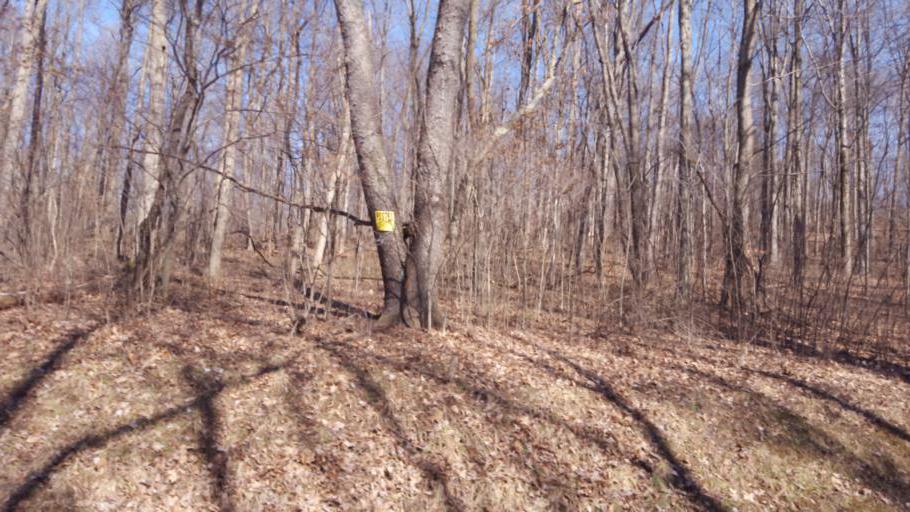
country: US
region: Ohio
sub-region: Ashland County
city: Loudonville
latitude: 40.5796
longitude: -82.3263
